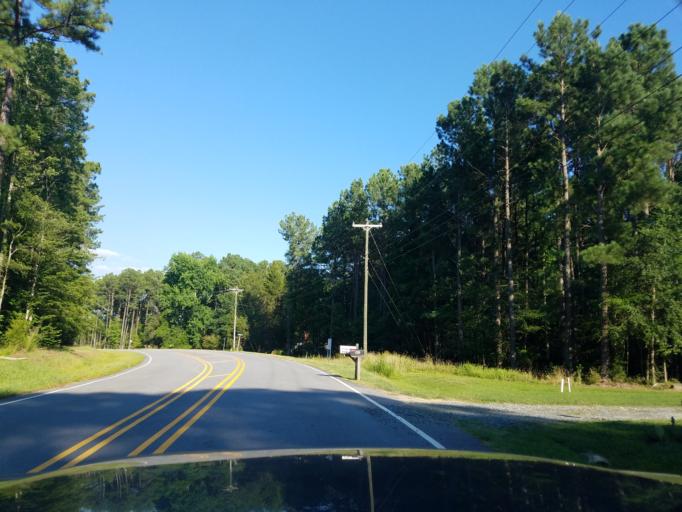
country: US
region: North Carolina
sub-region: Wake County
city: Green Level
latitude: 35.8751
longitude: -78.9374
